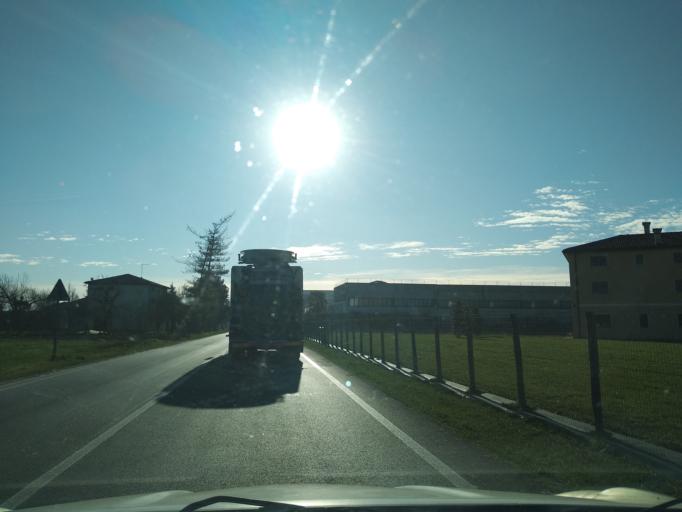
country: IT
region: Veneto
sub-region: Provincia di Vicenza
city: Quinto Vicentino
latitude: 45.5896
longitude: 11.6400
